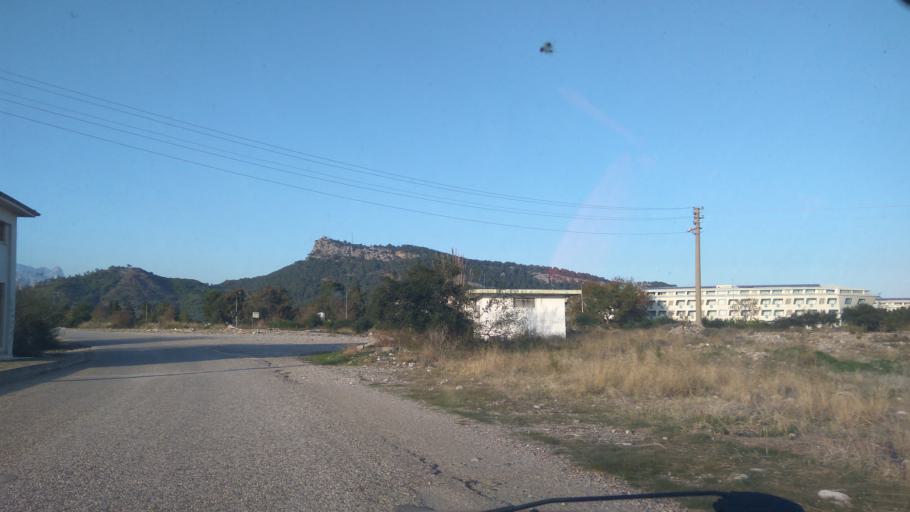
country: TR
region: Antalya
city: Kemer
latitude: 36.5639
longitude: 30.5712
